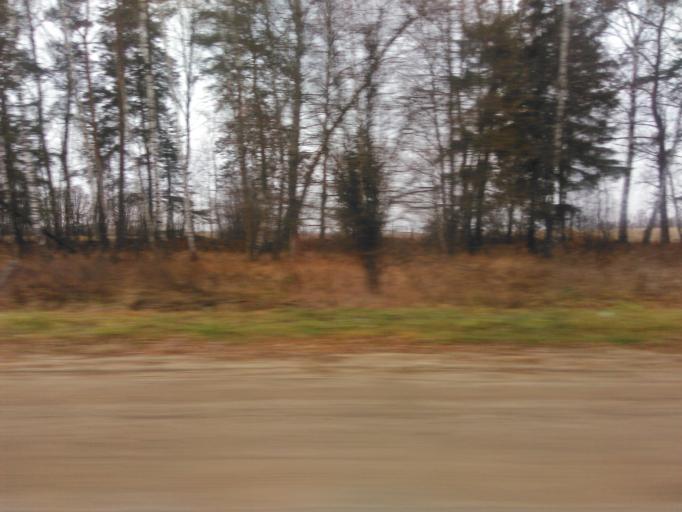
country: RU
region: Moskovskaya
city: Ashukino
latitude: 56.1301
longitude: 37.9764
